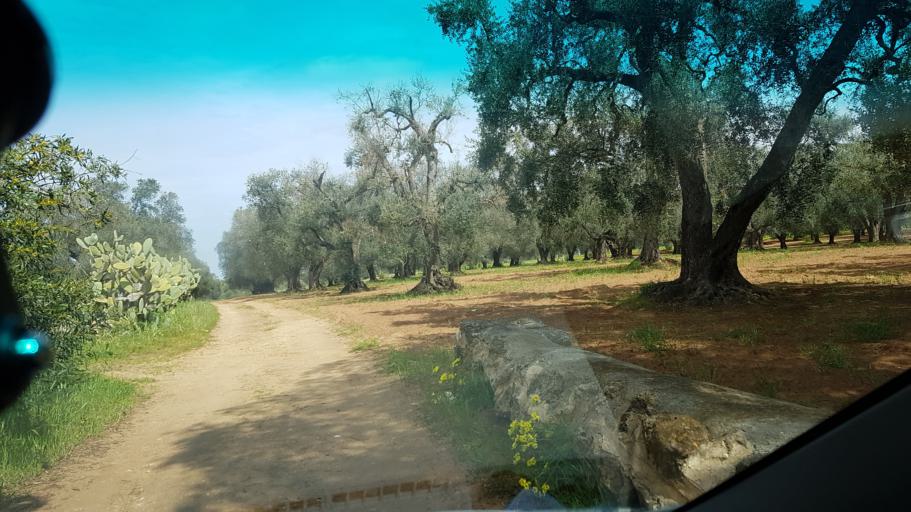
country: IT
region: Apulia
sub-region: Provincia di Brindisi
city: Mesagne
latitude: 40.6060
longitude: 17.8531
